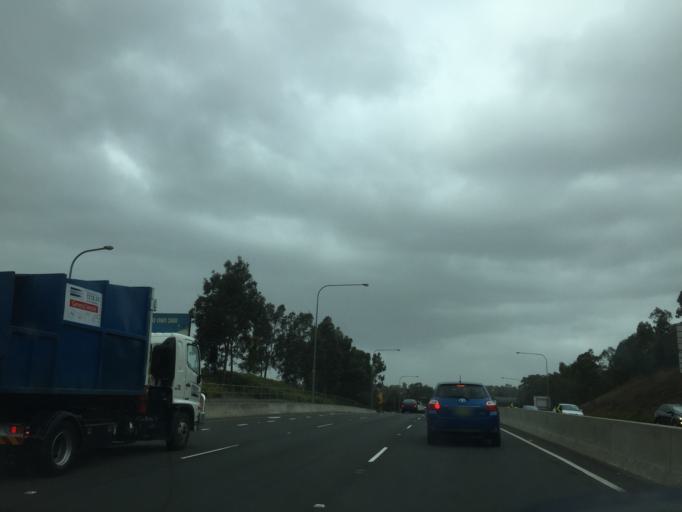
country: AU
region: New South Wales
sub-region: Blacktown
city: Stanhope Gardens
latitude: -33.7452
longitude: 150.9492
